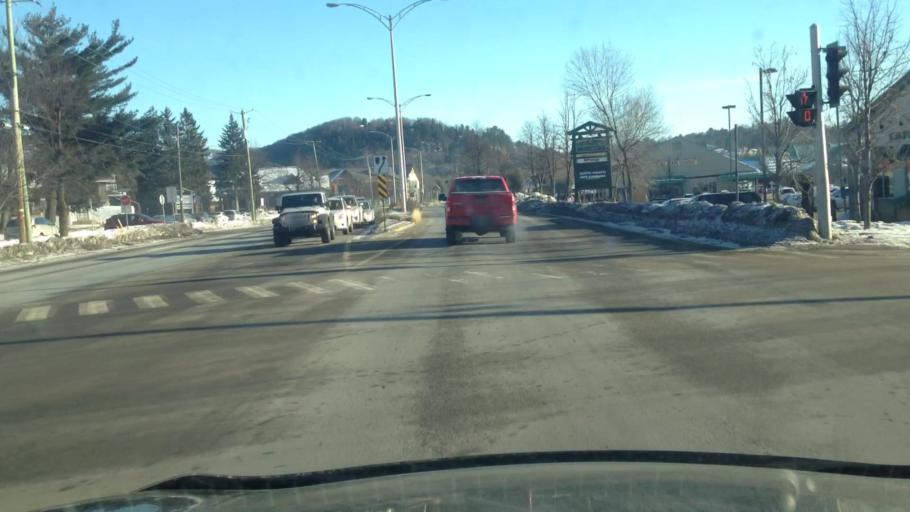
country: CA
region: Quebec
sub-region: Laurentides
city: Saint-Sauveur
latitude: 45.8915
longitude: -74.1578
